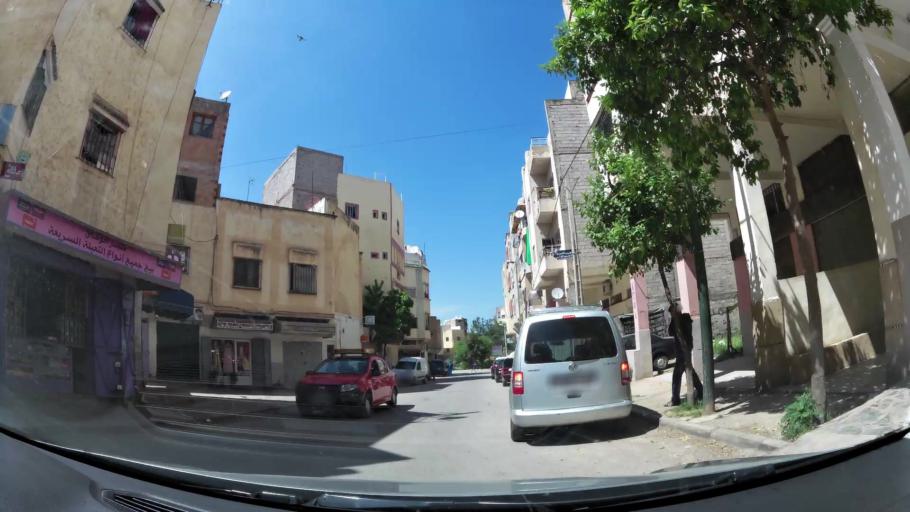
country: MA
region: Fes-Boulemane
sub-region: Fes
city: Fes
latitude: 34.0112
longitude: -5.0259
